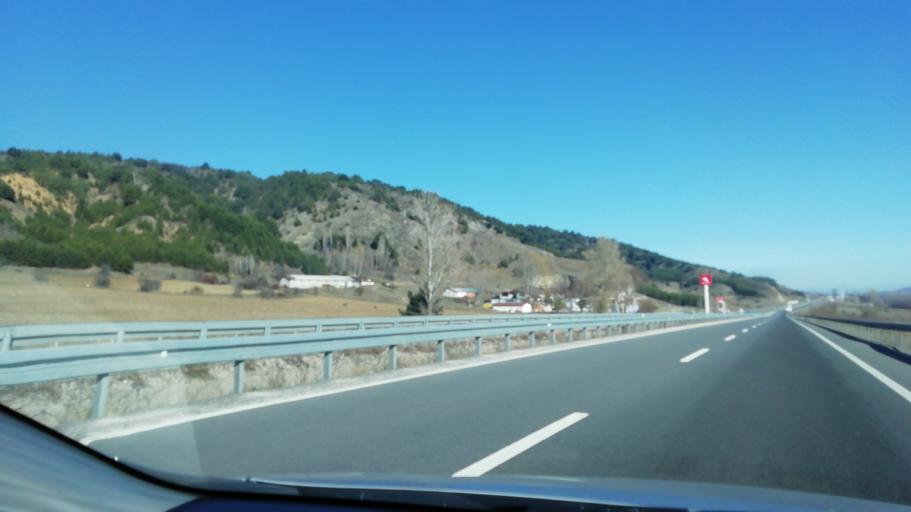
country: TR
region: Karabuk
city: Gozyeri
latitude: 40.8428
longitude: 32.4339
